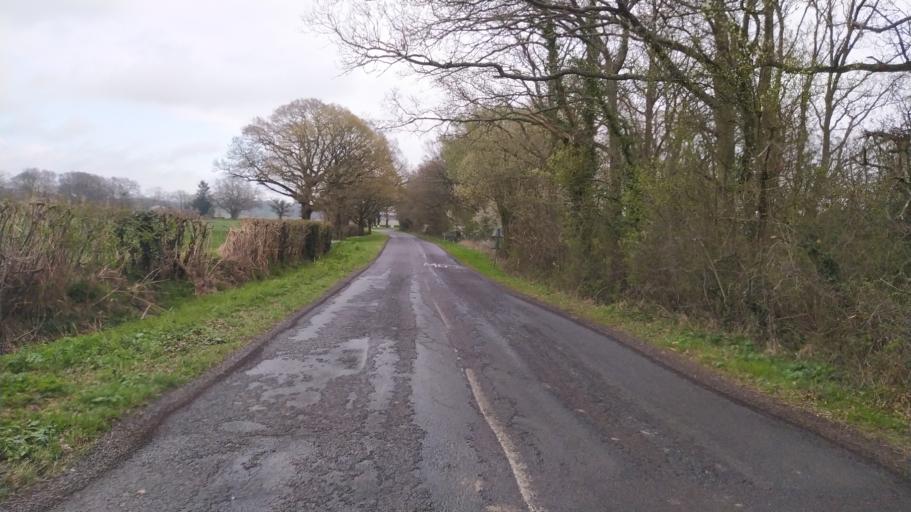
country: GB
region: England
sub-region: West Sussex
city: Petworth
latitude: 51.0274
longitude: -0.5911
